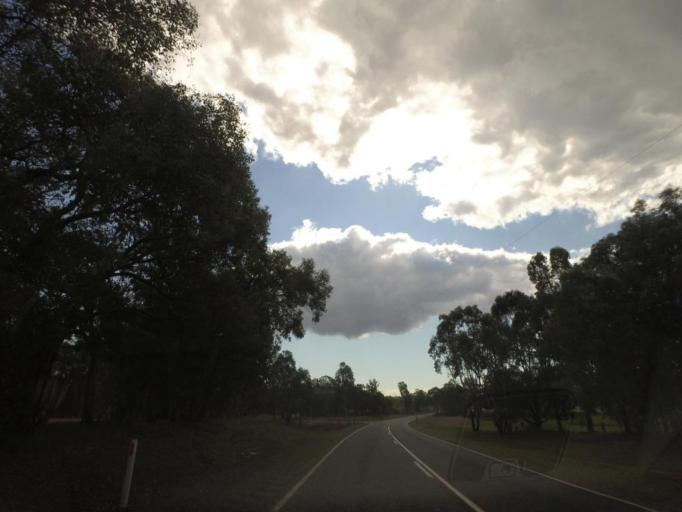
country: AU
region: New South Wales
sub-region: Corowa Shire
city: Howlong
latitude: -36.1829
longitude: 146.6072
